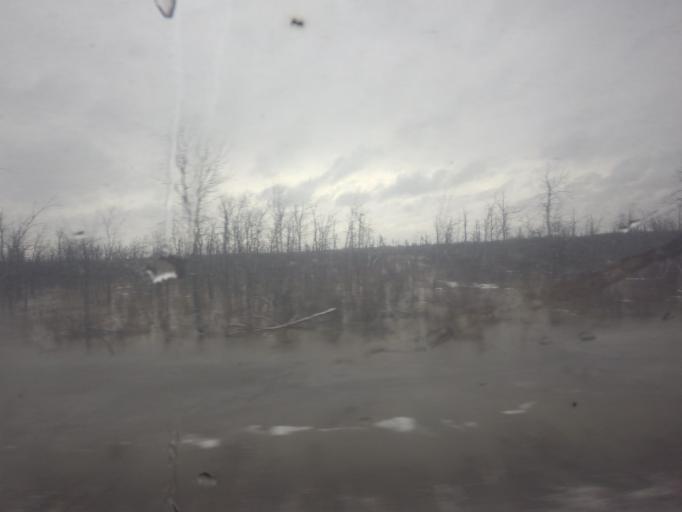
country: CA
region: Ontario
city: Bells Corners
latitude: 45.1620
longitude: -75.8372
